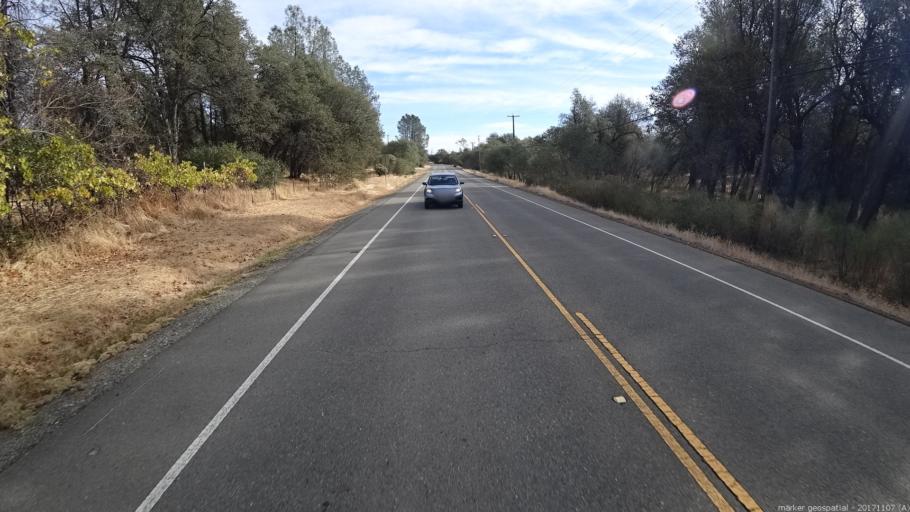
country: US
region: California
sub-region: Shasta County
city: Shasta
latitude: 40.5183
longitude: -122.4849
